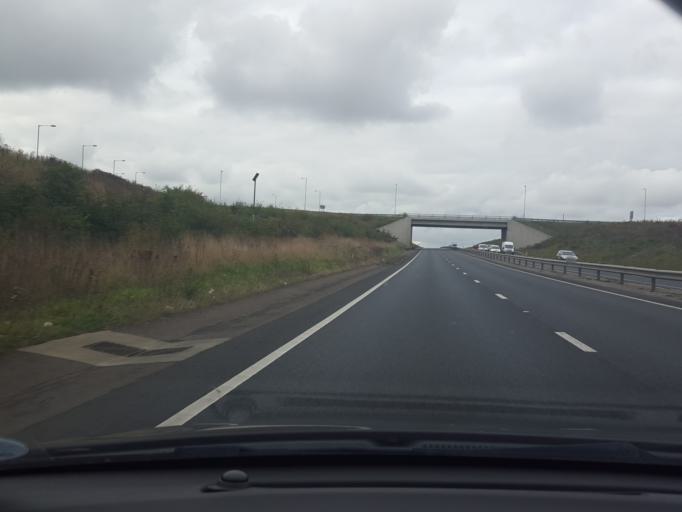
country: GB
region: England
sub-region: Suffolk
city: Stowmarket
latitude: 52.2045
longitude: 0.9773
